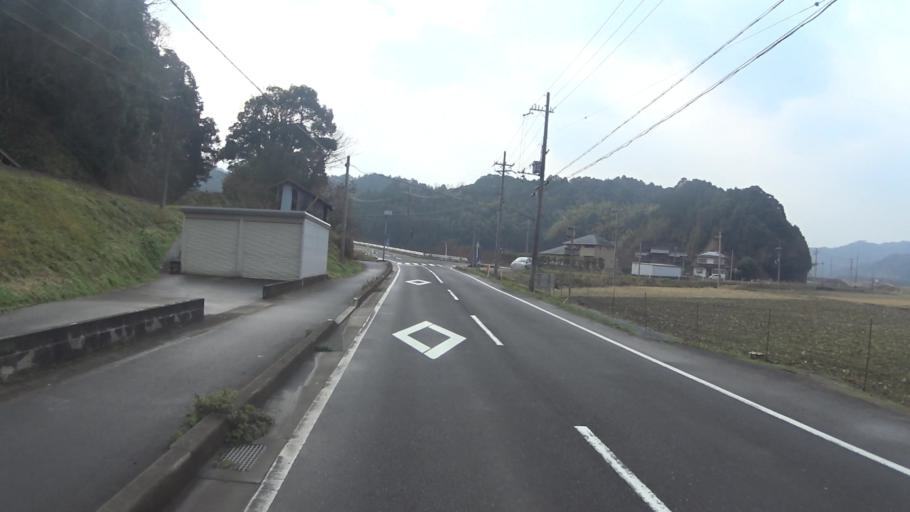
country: JP
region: Kyoto
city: Maizuru
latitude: 35.4568
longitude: 135.2846
